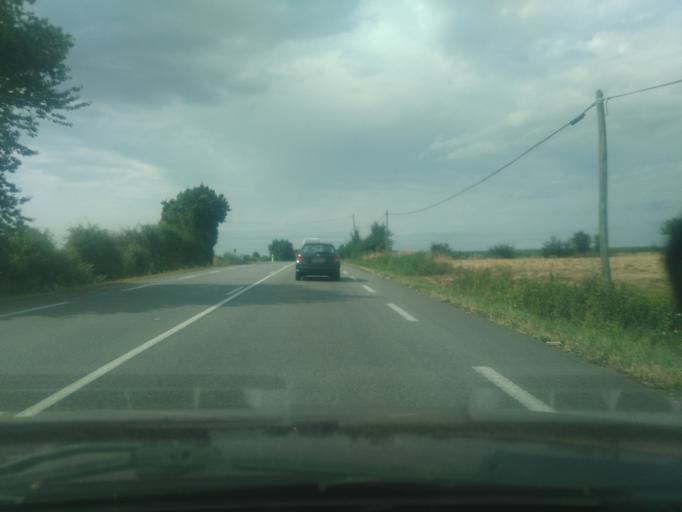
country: FR
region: Pays de la Loire
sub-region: Departement de la Vendee
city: Sainte-Cecile
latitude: 46.7822
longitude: -1.1181
